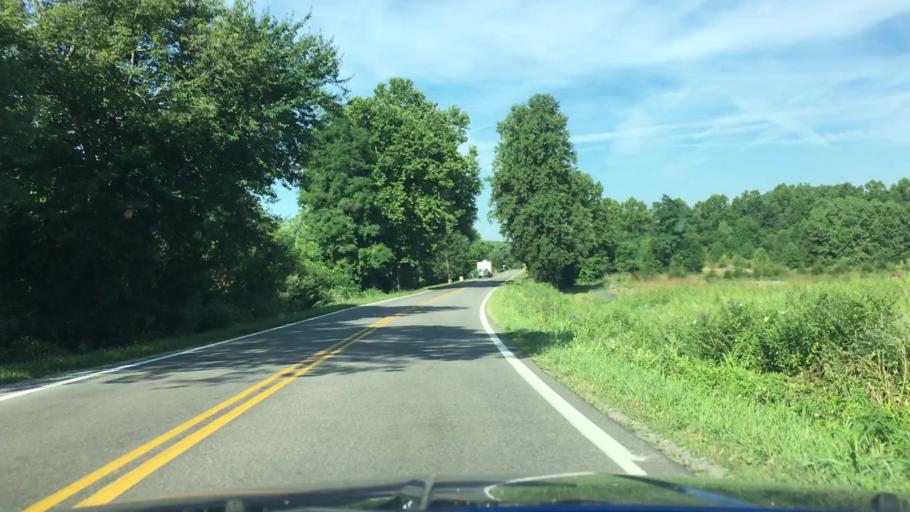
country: US
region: Virginia
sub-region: Augusta County
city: Lyndhurst
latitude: 38.0294
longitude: -78.9289
